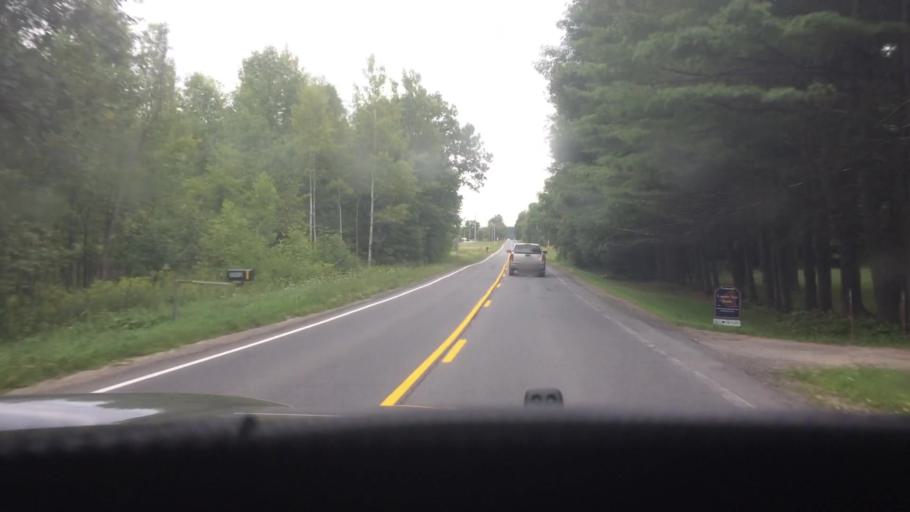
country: US
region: New York
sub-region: St. Lawrence County
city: Canton
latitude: 44.5466
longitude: -75.1500
